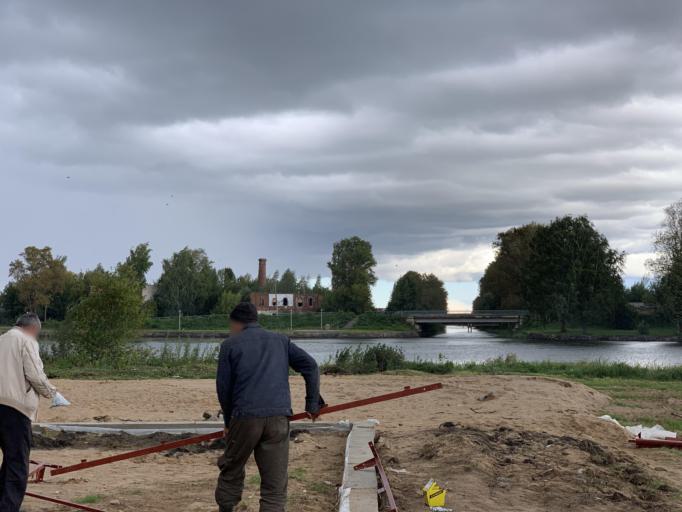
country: RU
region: Tverskaya
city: Vyshniy Volochek
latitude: 57.5787
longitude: 34.5540
